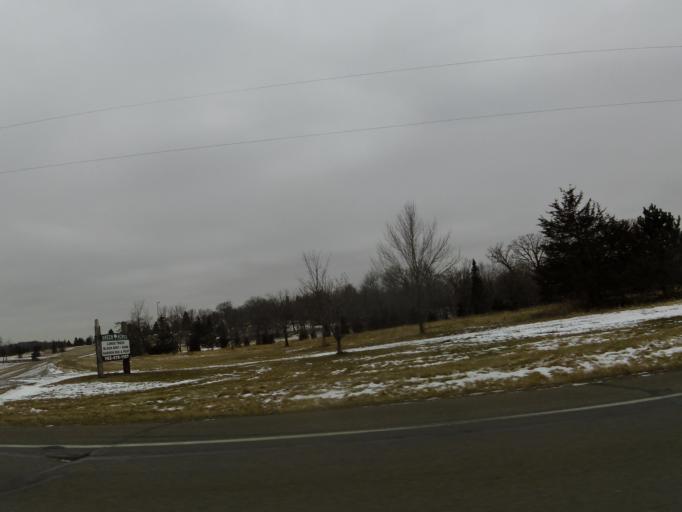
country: US
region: Minnesota
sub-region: Hennepin County
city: Independence
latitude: 45.0143
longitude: -93.6934
